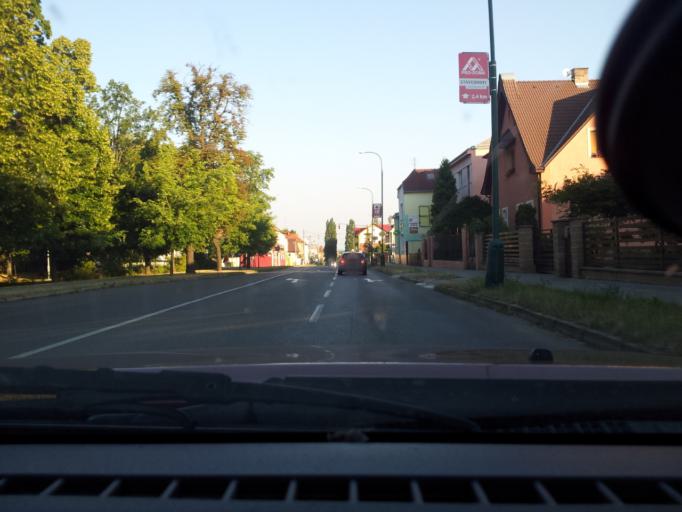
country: CZ
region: South Moravian
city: Hodonin
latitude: 48.8602
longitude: 17.1206
